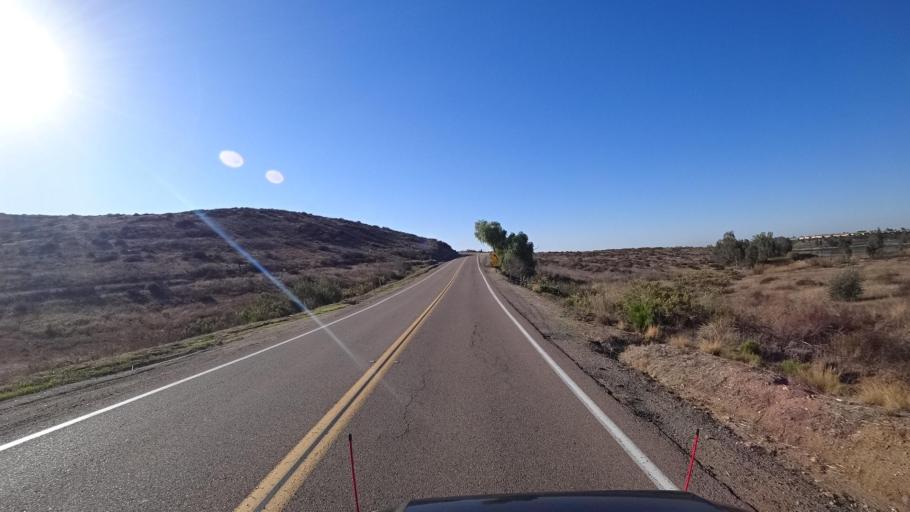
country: US
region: California
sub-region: San Diego County
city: Jamul
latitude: 32.6384
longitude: -116.9224
